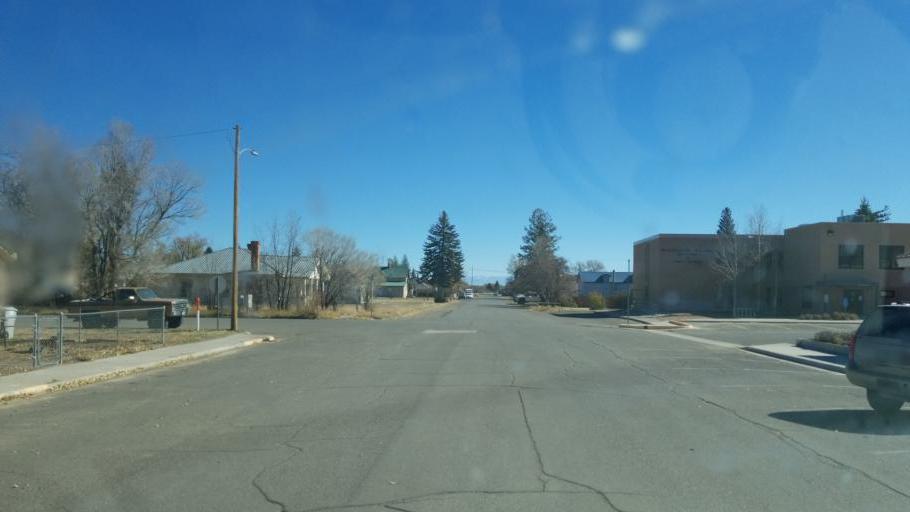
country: US
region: Colorado
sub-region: Rio Grande County
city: Del Norte
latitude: 37.6774
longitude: -106.3498
